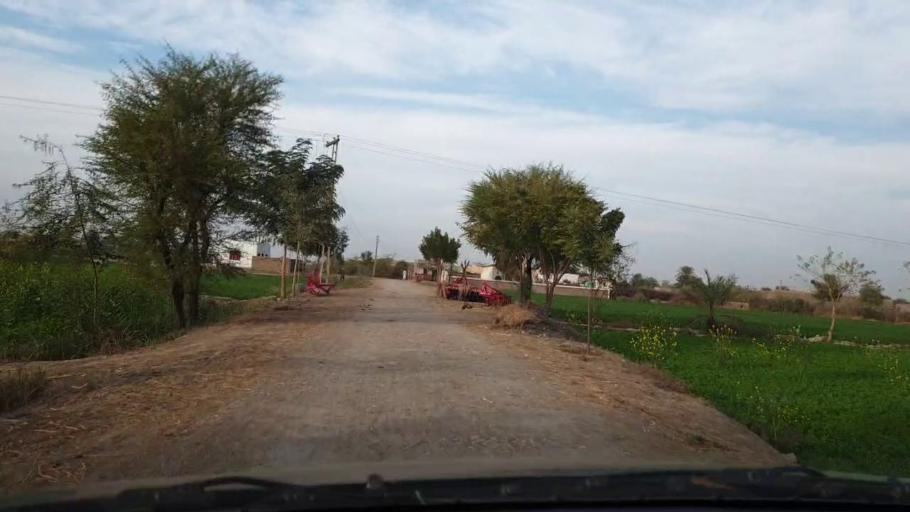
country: PK
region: Sindh
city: Khadro
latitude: 26.1570
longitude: 68.7357
